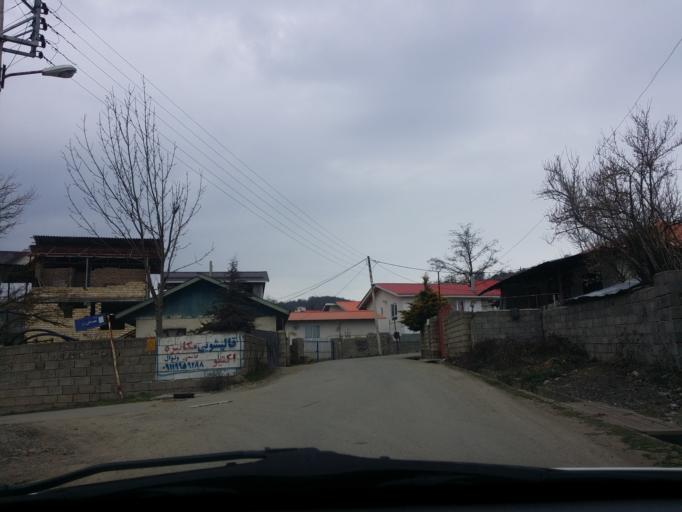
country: IR
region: Mazandaran
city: `Abbasabad
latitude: 36.5484
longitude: 51.1651
